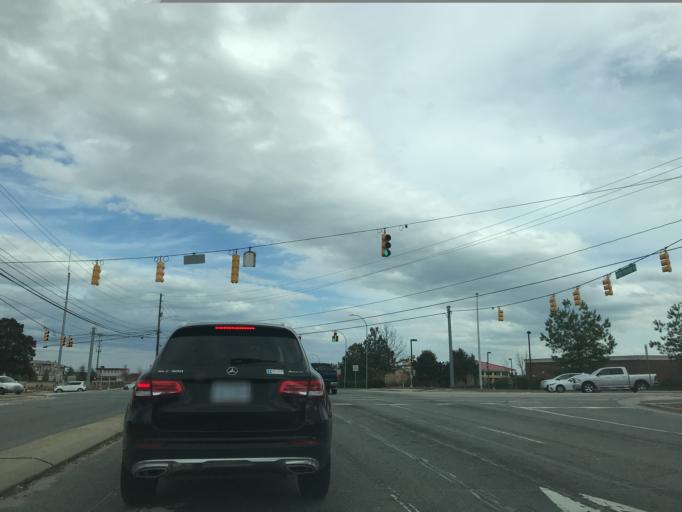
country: US
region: North Carolina
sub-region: Wake County
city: Morrisville
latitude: 35.7913
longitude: -78.8478
